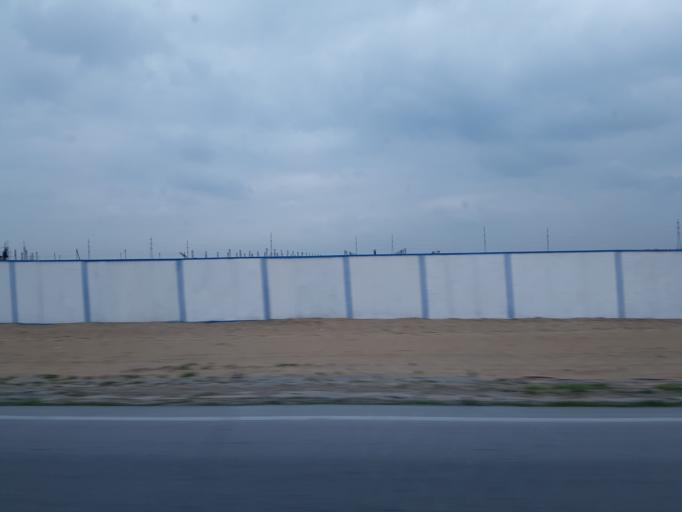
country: TM
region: Ahal
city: Ashgabat
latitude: 38.0412
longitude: 58.4044
